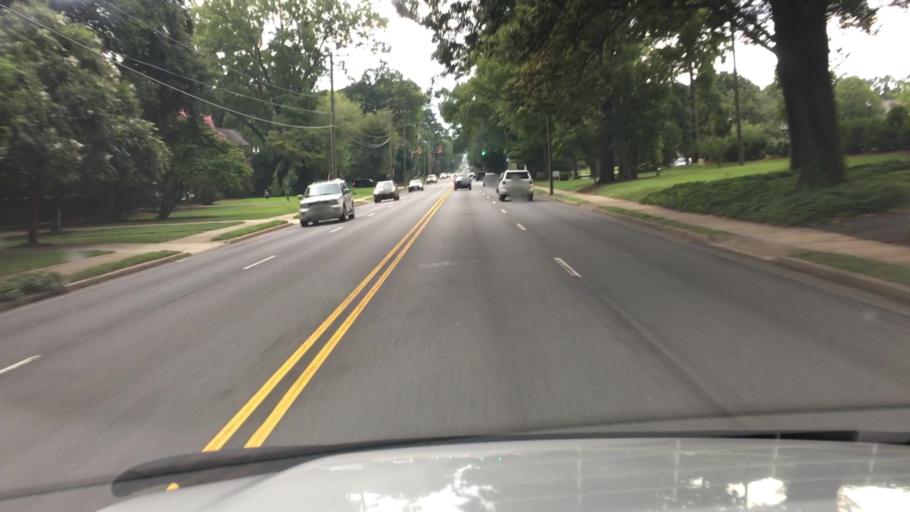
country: US
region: North Carolina
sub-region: Mecklenburg County
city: Charlotte
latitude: 35.1899
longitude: -80.8231
